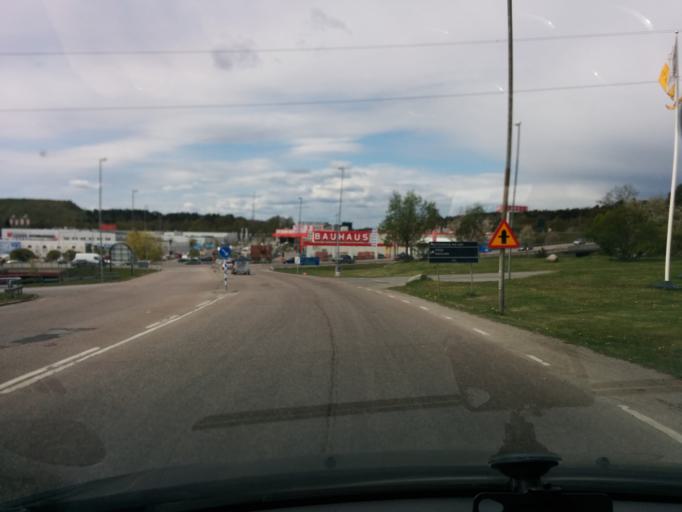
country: SE
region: Stockholm
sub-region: Botkyrka Kommun
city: Alby
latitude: 59.2390
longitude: 17.8392
